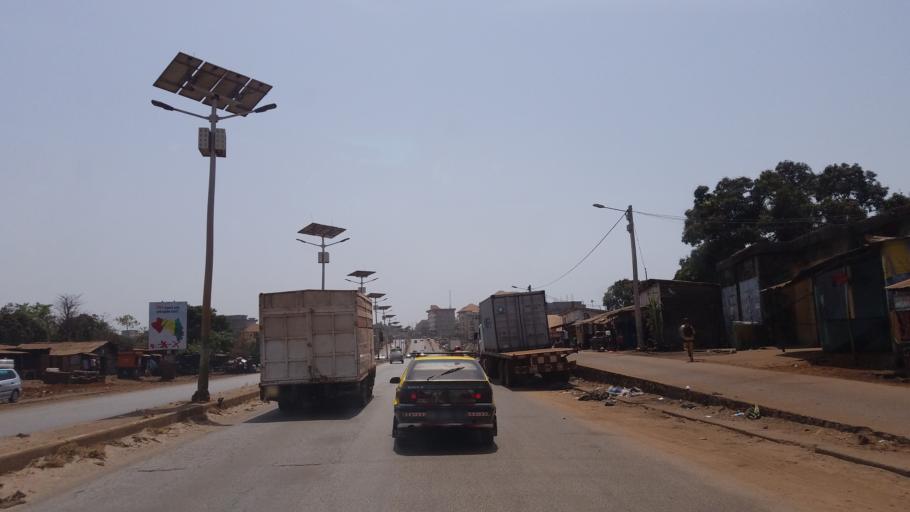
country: GN
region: Conakry
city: Conakry
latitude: 9.6508
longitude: -13.5812
